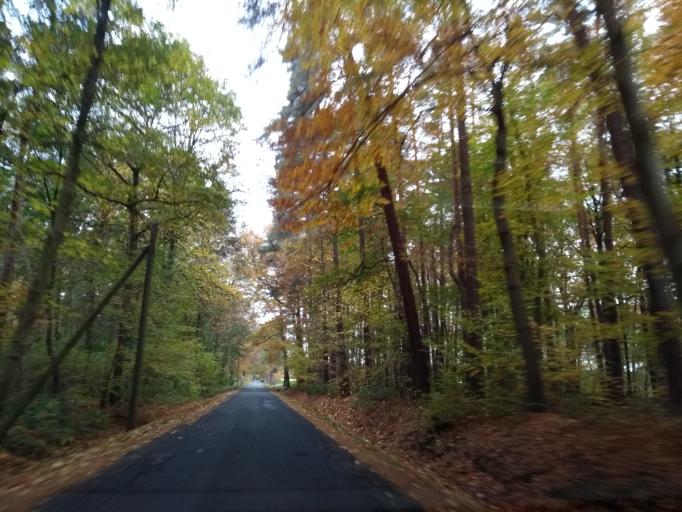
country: DE
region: North Rhine-Westphalia
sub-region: Regierungsbezirk Detmold
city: Hovelhof
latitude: 51.7801
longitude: 8.6882
